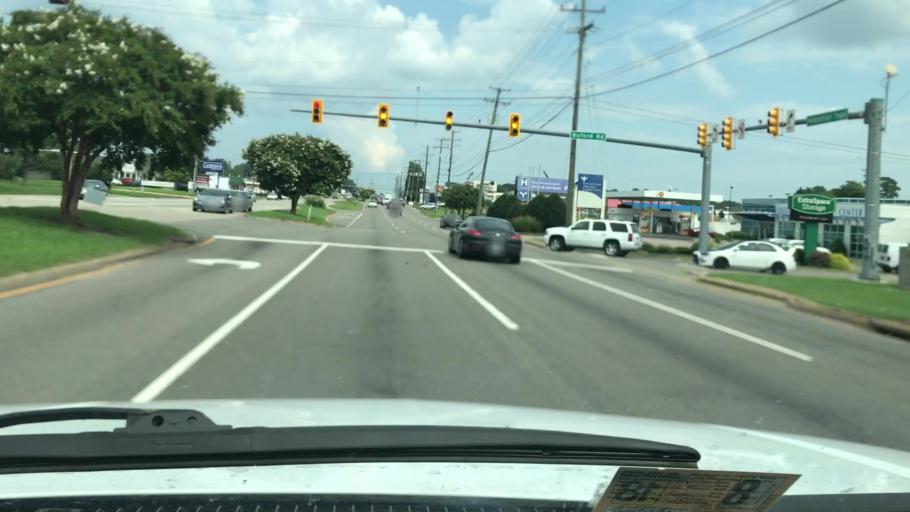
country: US
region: Virginia
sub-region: Chesterfield County
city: Bon Air
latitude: 37.4974
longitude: -77.5454
